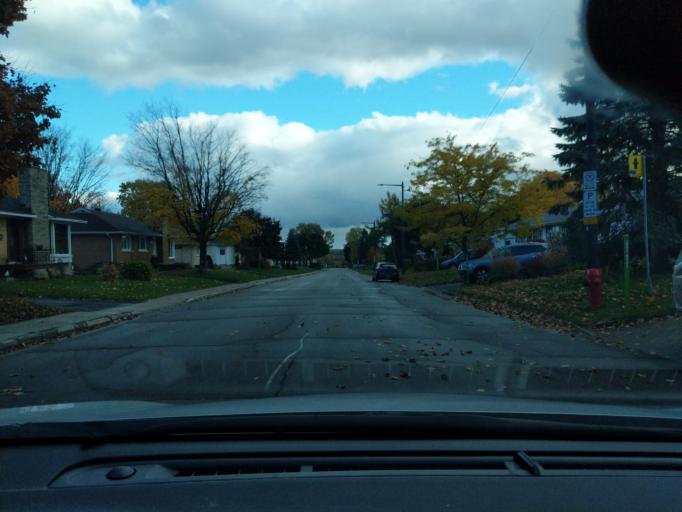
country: CA
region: Quebec
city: L'Ancienne-Lorette
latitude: 46.7639
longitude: -71.2866
